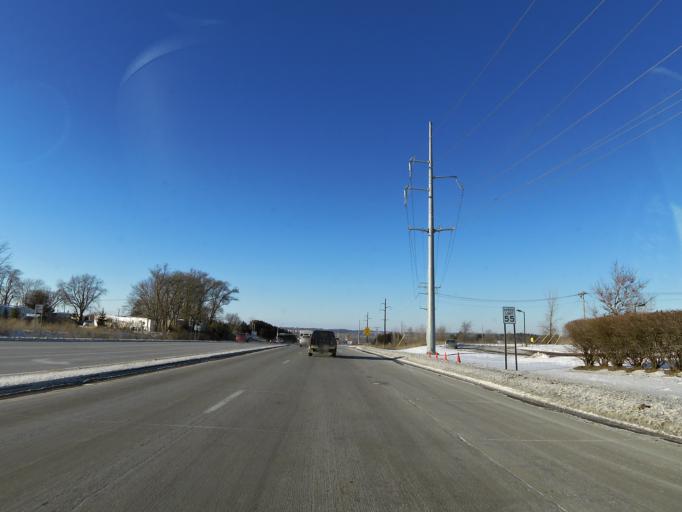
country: US
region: Minnesota
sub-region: Carver County
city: Chaska
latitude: 44.7665
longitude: -93.5793
